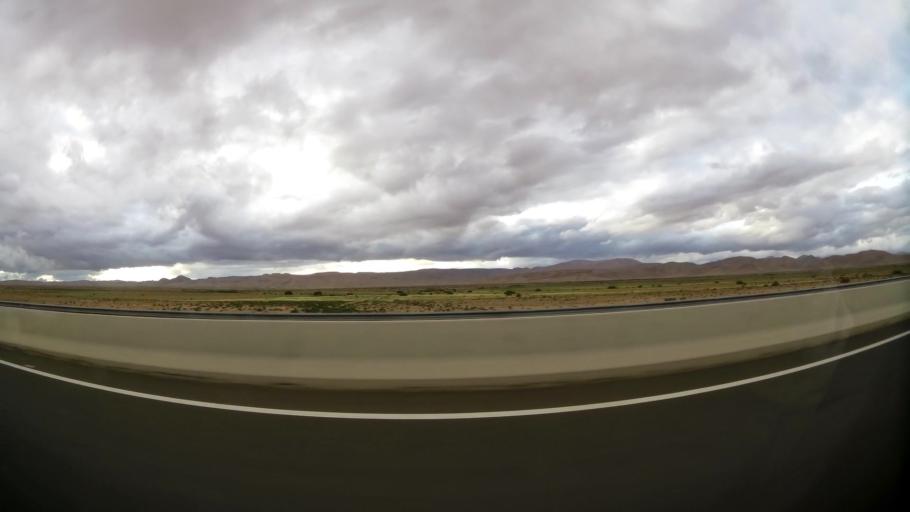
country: MA
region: Taza-Al Hoceima-Taounate
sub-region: Taza
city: Guercif
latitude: 34.3149
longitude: -3.5917
